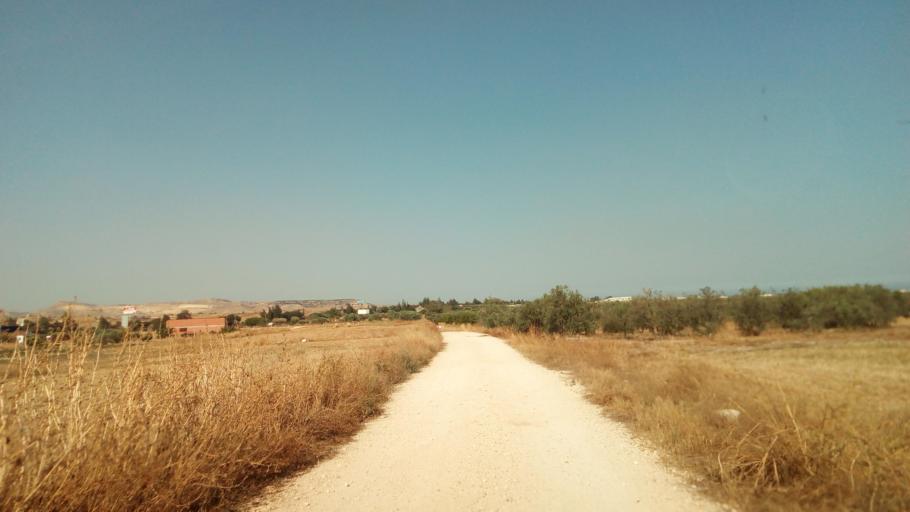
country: CY
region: Larnaka
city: Aradippou
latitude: 34.9607
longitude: 33.5976
